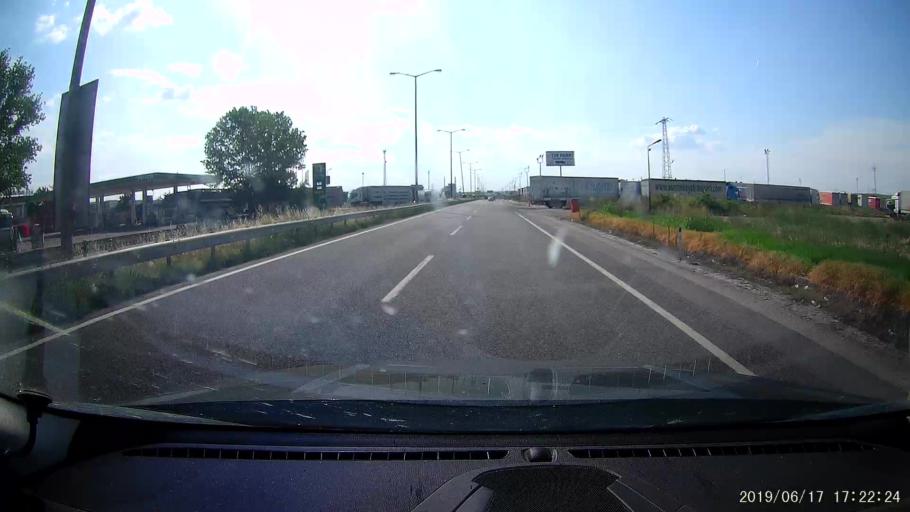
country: GR
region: East Macedonia and Thrace
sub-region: Nomos Evrou
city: Rizia
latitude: 41.7114
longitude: 26.3754
